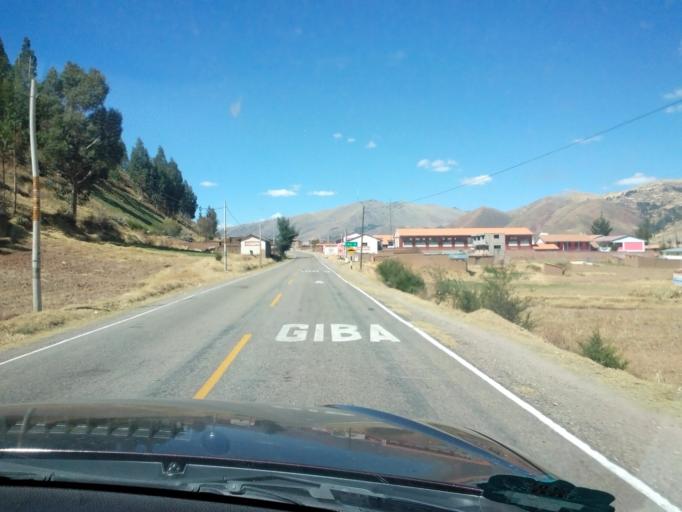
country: PE
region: Cusco
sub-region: Provincia de Canchis
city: Tinta
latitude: -14.1391
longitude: -71.4034
